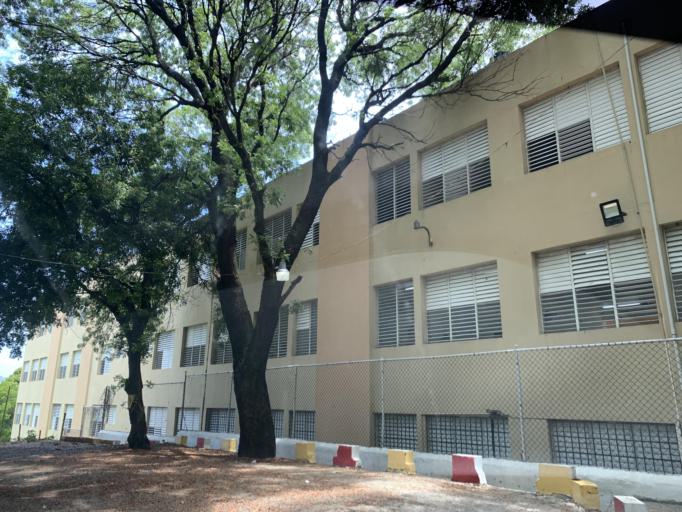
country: DO
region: Puerto Plata
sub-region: Puerto Plata
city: Puerto Plata
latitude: 19.7889
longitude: -70.6919
